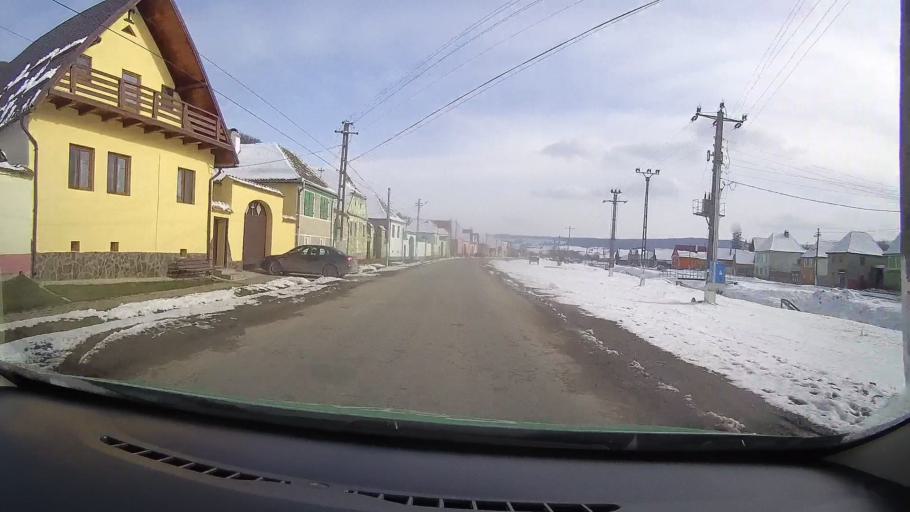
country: RO
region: Sibiu
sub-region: Comuna Iacobeni
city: Iacobeni
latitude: 46.0502
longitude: 24.7186
